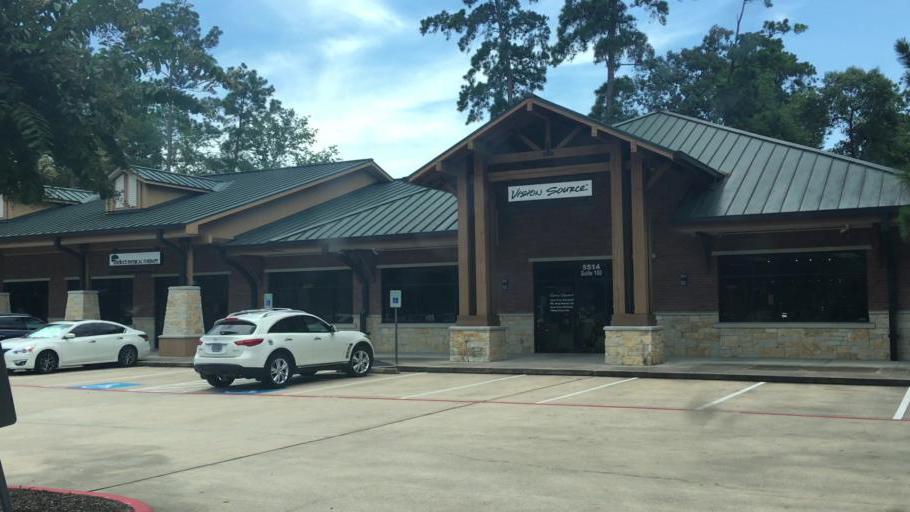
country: US
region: Texas
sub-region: Harris County
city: Atascocita
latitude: 29.9889
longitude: -95.1891
